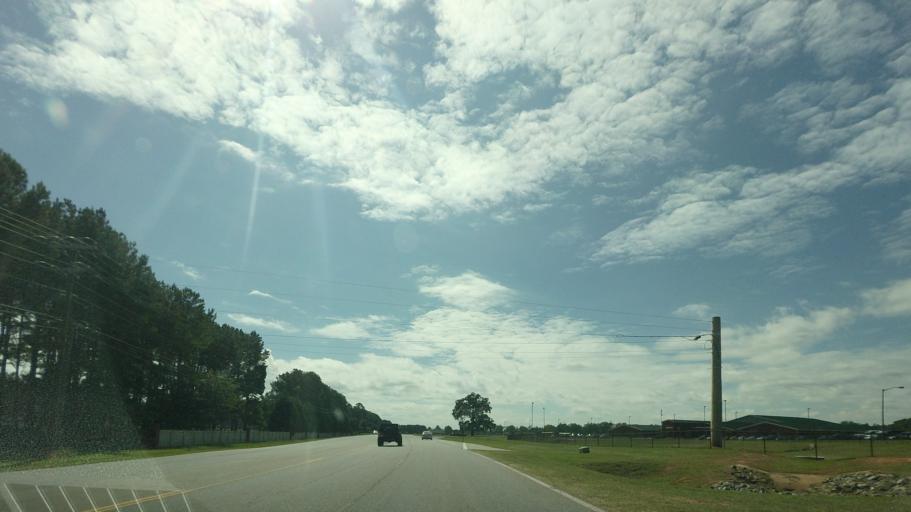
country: US
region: Georgia
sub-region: Houston County
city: Centerville
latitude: 32.5776
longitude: -83.6941
